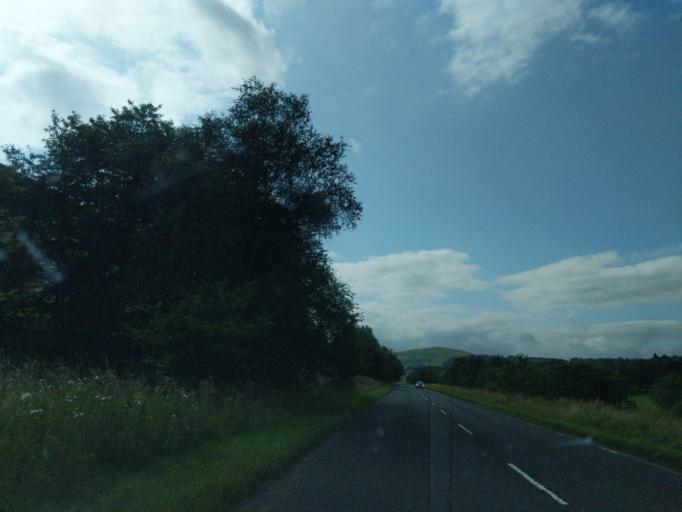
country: GB
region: Scotland
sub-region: The Scottish Borders
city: Peebles
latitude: 55.6971
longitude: -3.2126
